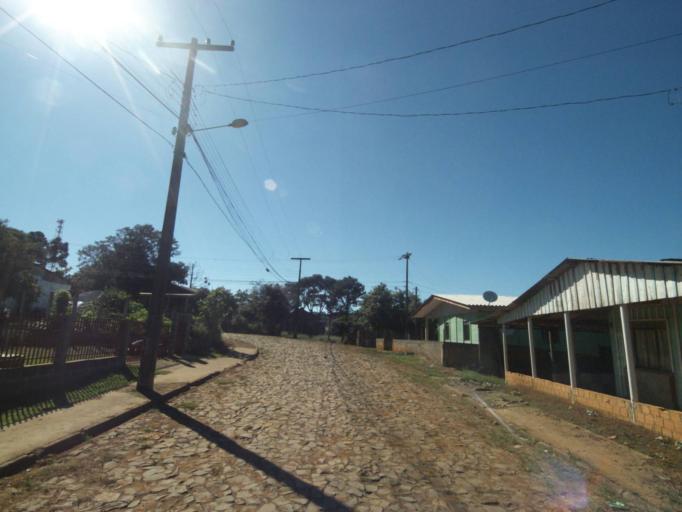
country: BR
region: Parana
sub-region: Pinhao
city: Pinhao
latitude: -25.8388
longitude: -52.0313
